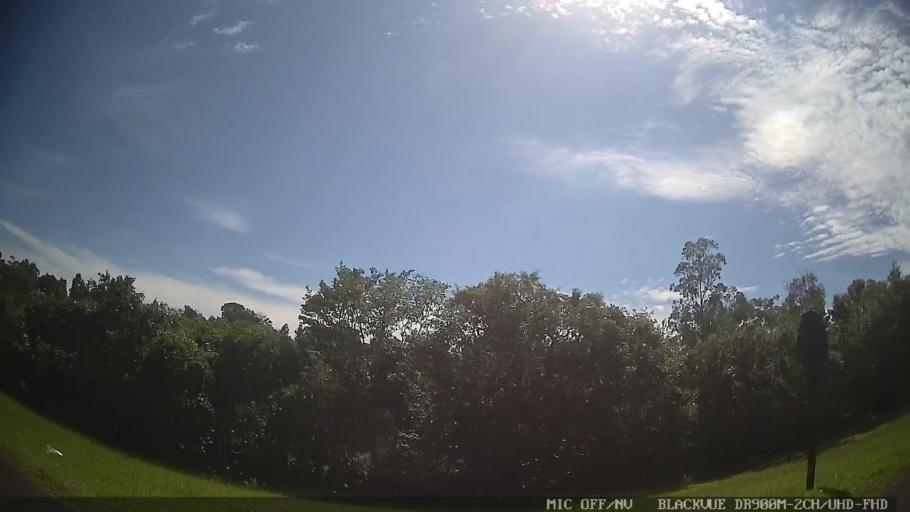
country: BR
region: Sao Paulo
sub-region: Tiete
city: Tiete
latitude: -23.1628
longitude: -47.6476
